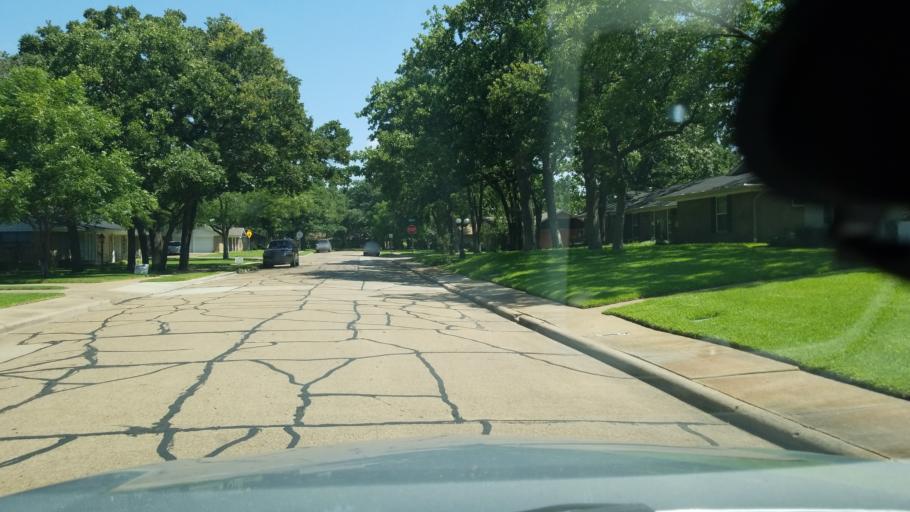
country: US
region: Texas
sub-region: Dallas County
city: Irving
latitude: 32.8329
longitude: -96.9533
